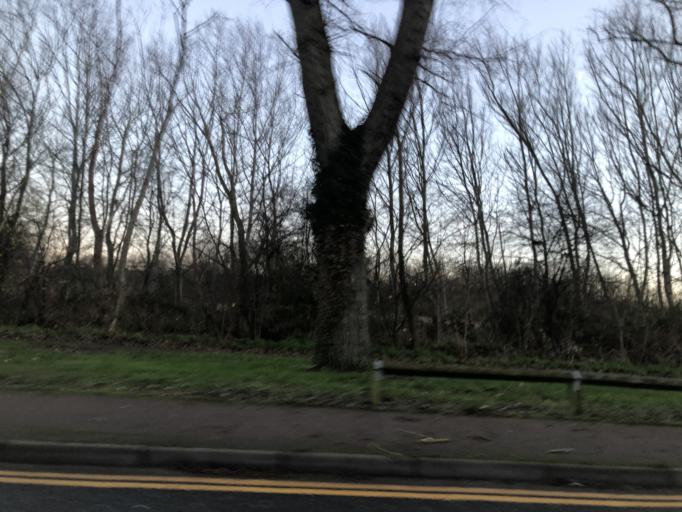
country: GB
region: England
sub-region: Greater London
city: Woolwich
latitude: 51.4758
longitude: 0.0495
